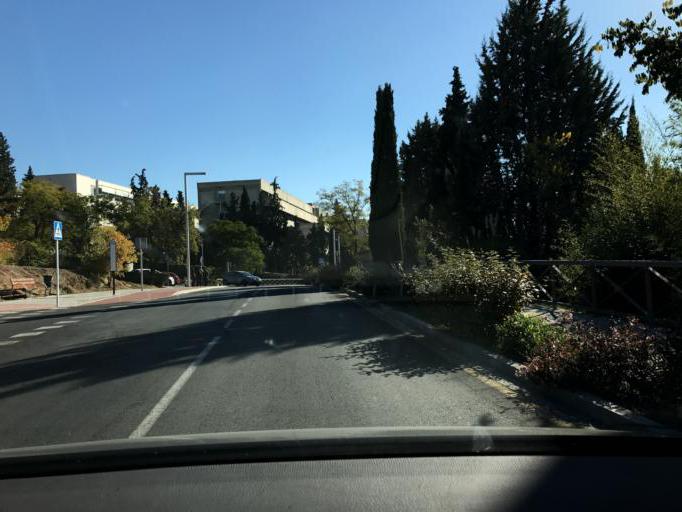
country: ES
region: Andalusia
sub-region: Provincia de Granada
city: Granada
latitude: 37.1938
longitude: -3.5951
